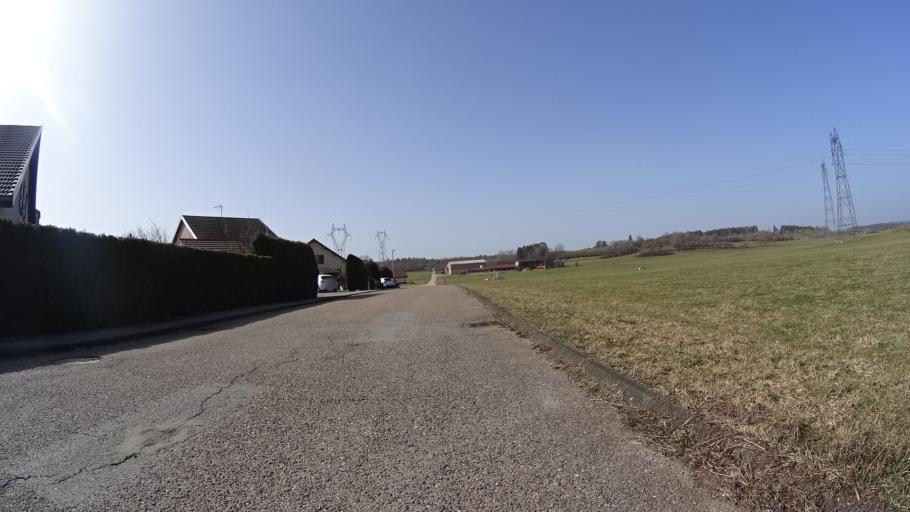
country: FR
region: Franche-Comte
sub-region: Departement du Doubs
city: Frasne
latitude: 46.8534
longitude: 6.1483
